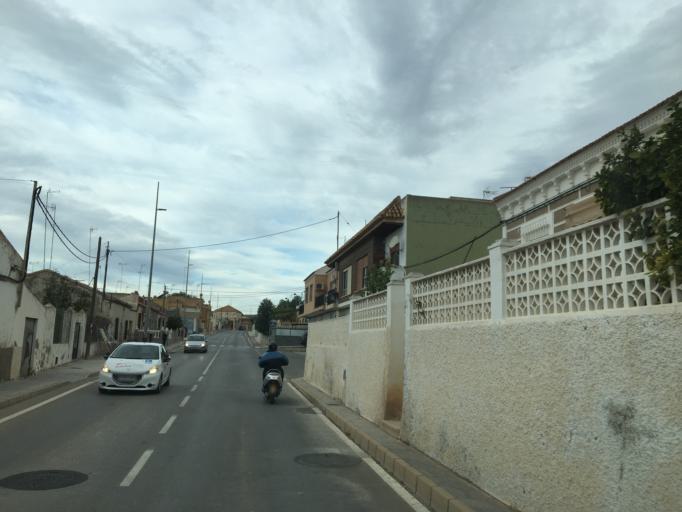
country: ES
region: Murcia
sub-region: Murcia
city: Cartagena
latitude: 37.6118
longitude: -1.0457
